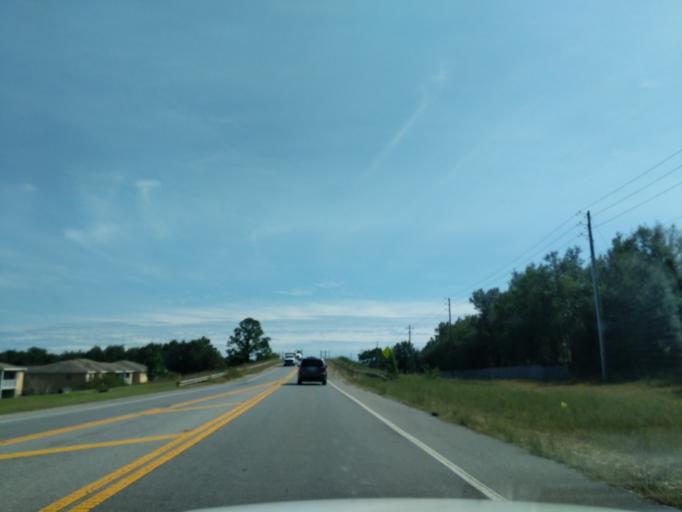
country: US
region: Florida
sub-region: Okaloosa County
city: Crestview
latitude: 30.7176
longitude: -86.6120
